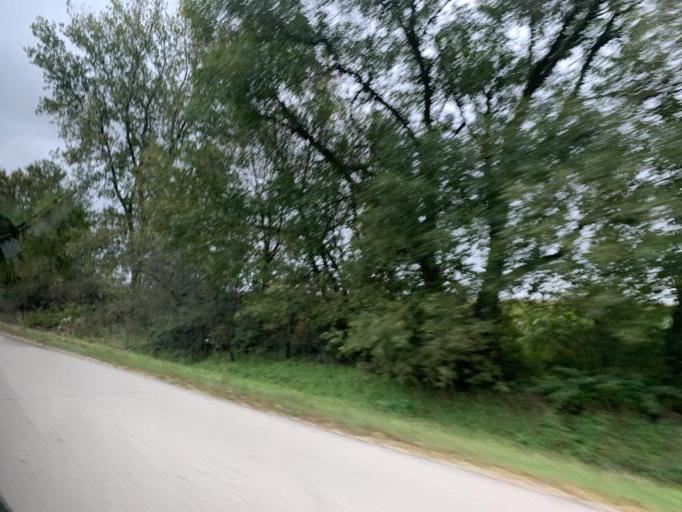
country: US
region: Wisconsin
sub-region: Sauk County
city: Prairie du Sac
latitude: 43.2996
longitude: -89.7789
